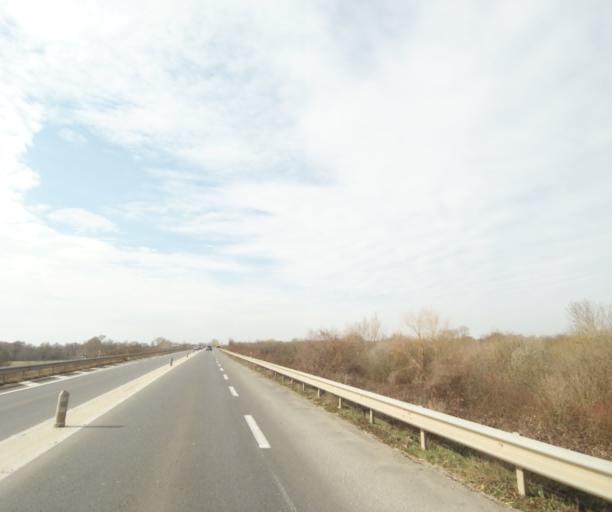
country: FR
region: Poitou-Charentes
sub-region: Departement des Deux-Sevres
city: Aiffres
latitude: 46.2982
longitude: -0.4418
